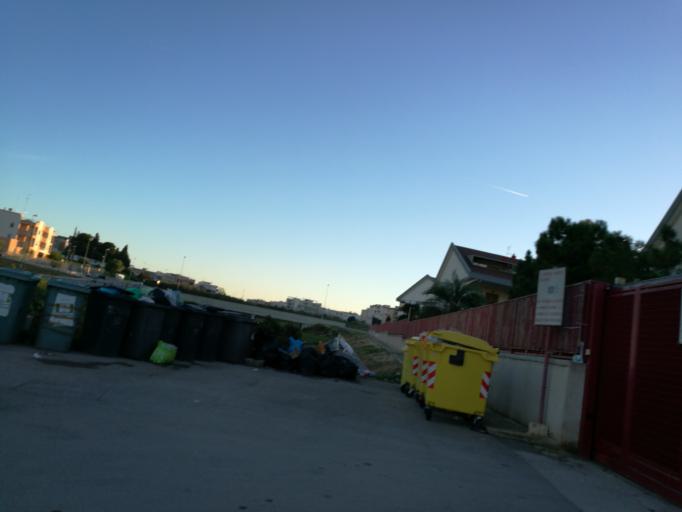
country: IT
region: Apulia
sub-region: Provincia di Bari
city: Adelfia
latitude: 41.0080
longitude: 16.8740
